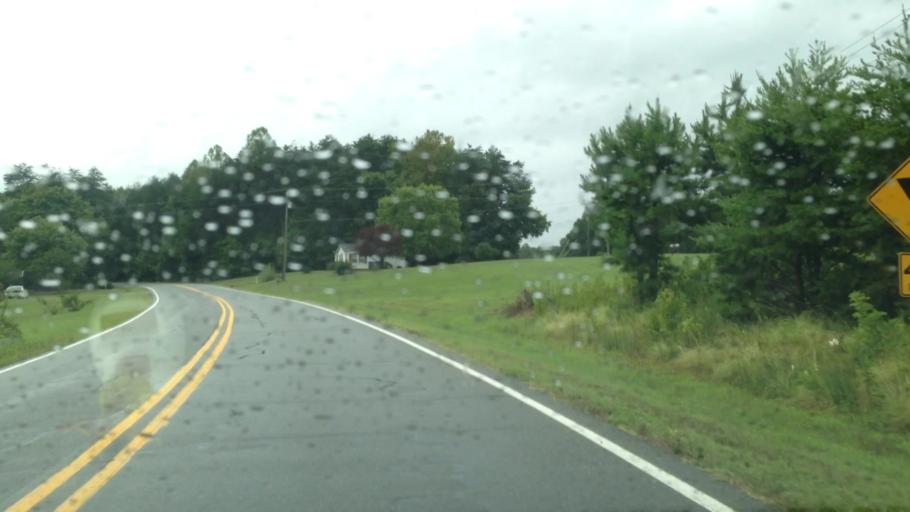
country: US
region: North Carolina
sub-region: Stokes County
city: Walnut Cove
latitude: 36.2634
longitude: -80.0995
